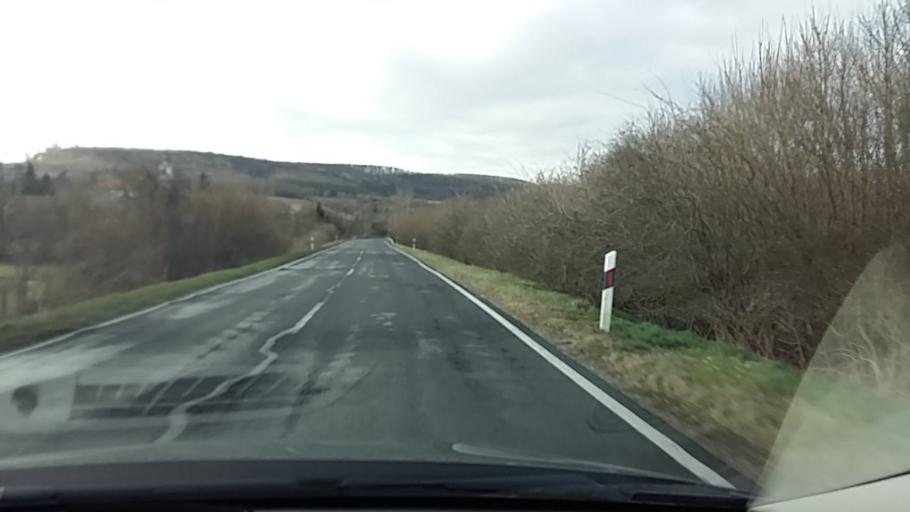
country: HU
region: Veszprem
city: Zanka
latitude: 46.9646
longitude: 17.6242
